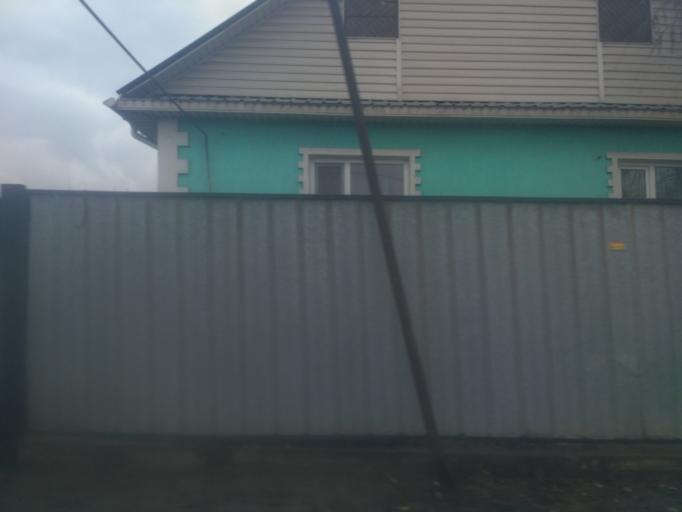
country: KZ
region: Almaty Oblysy
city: Burunday
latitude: 43.2159
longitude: 76.7446
